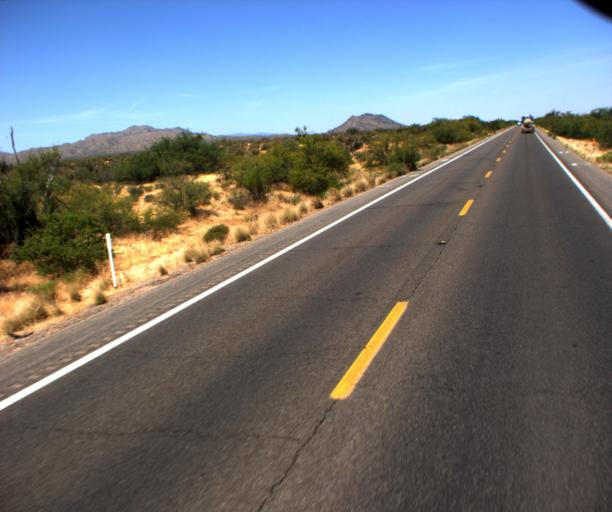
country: US
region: Arizona
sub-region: Gila County
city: Peridot
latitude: 33.3108
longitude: -110.5058
